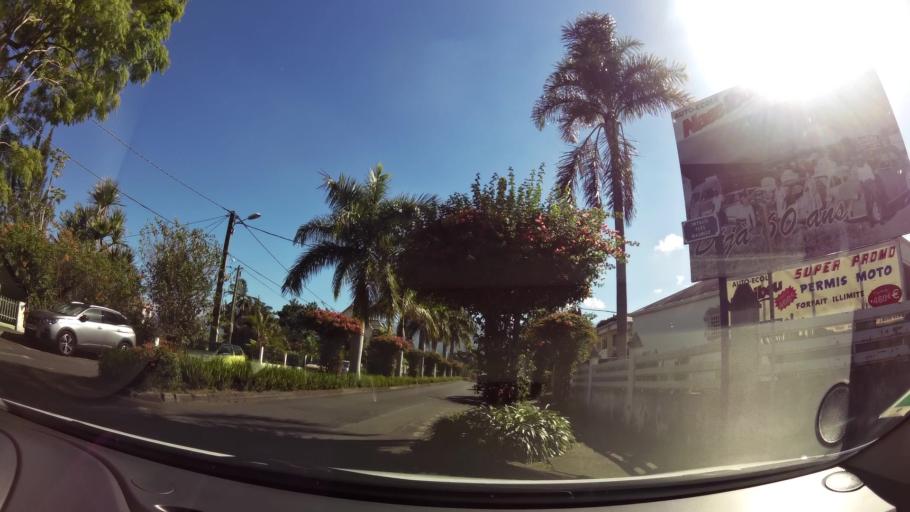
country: RE
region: Reunion
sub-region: Reunion
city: Le Tampon
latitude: -21.2684
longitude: 55.5131
